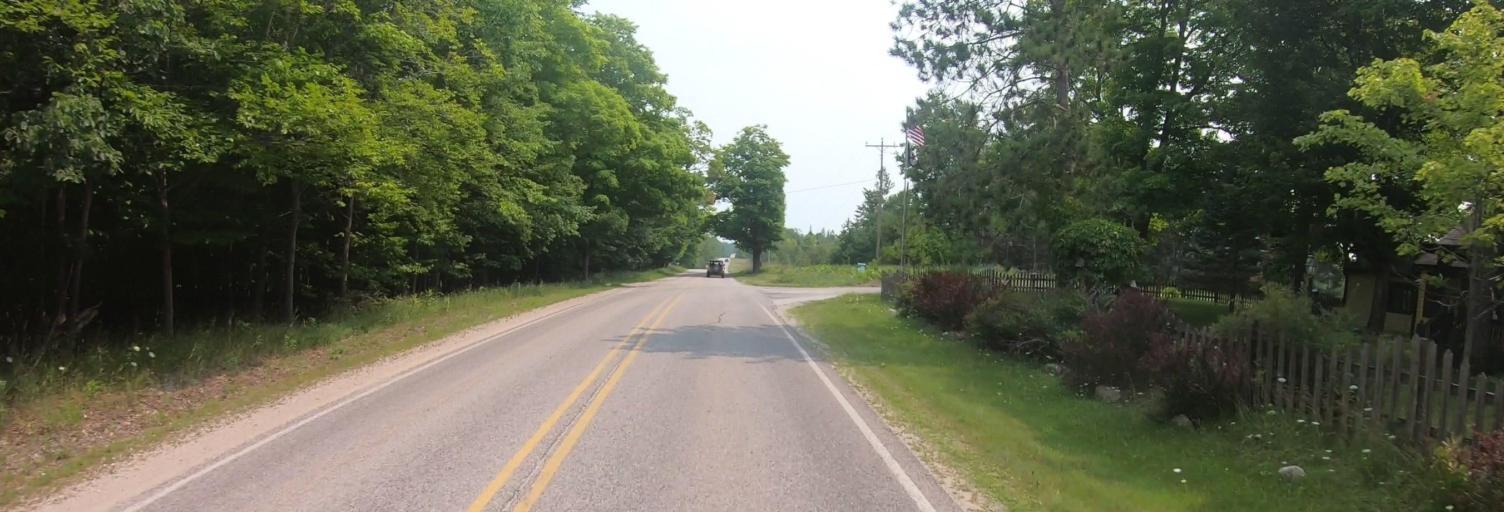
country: CA
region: Ontario
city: Thessalon
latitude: 45.9987
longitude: -83.7237
